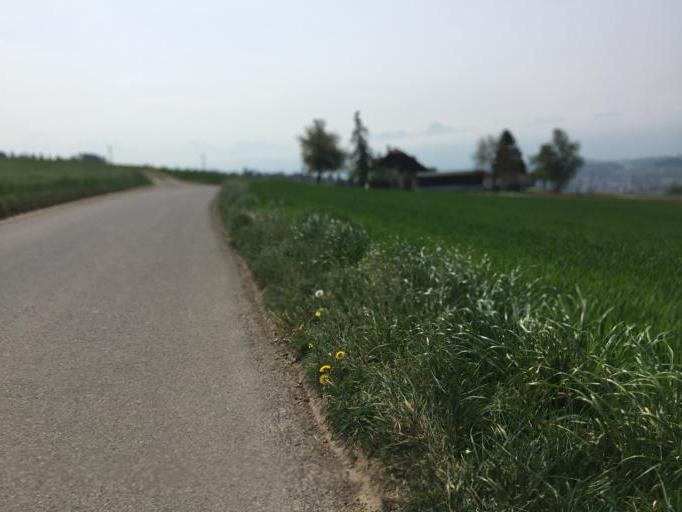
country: CH
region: Bern
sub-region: Bern-Mittelland District
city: Taegertschi
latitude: 46.8633
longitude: 7.5818
